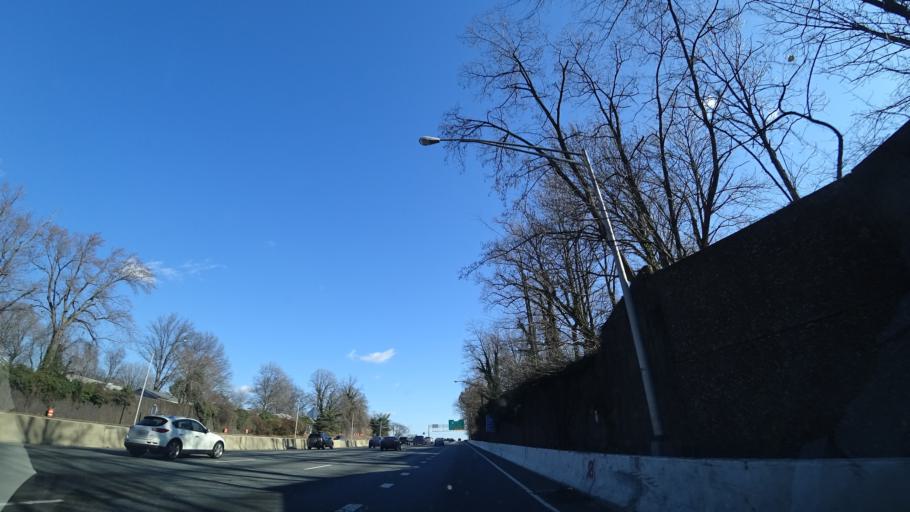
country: US
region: Maryland
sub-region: Montgomery County
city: Forest Glen
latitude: 39.0131
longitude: -77.0476
